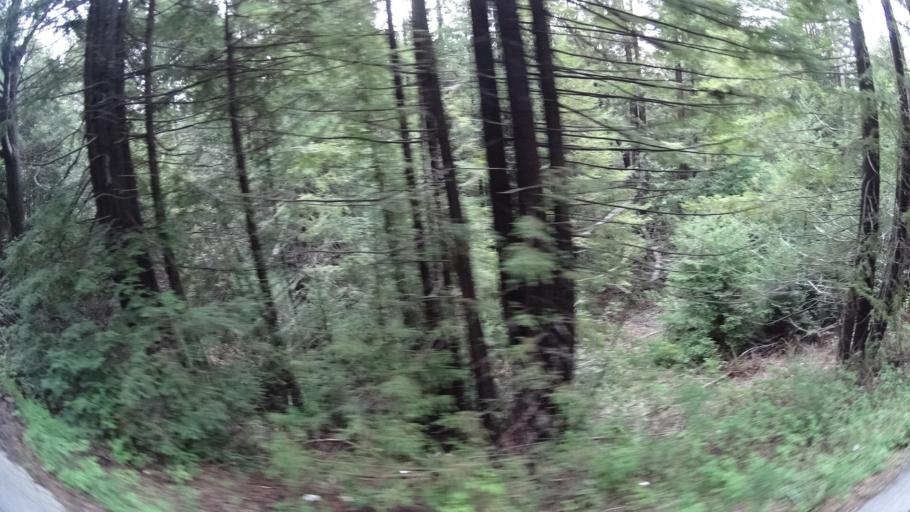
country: US
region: California
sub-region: Humboldt County
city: Redway
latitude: 40.2884
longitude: -123.8361
